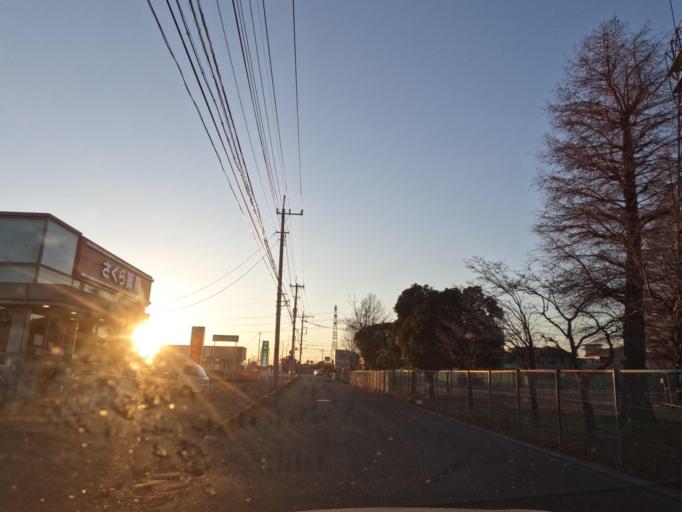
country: JP
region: Saitama
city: Kasukabe
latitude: 35.9626
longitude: 139.7481
